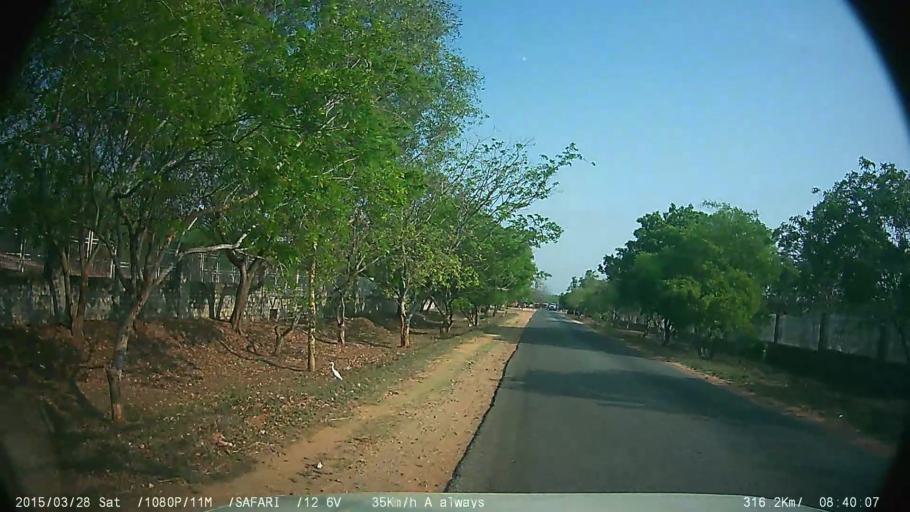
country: IN
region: Karnataka
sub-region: Mysore
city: Mysore
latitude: 12.3650
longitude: 76.5810
